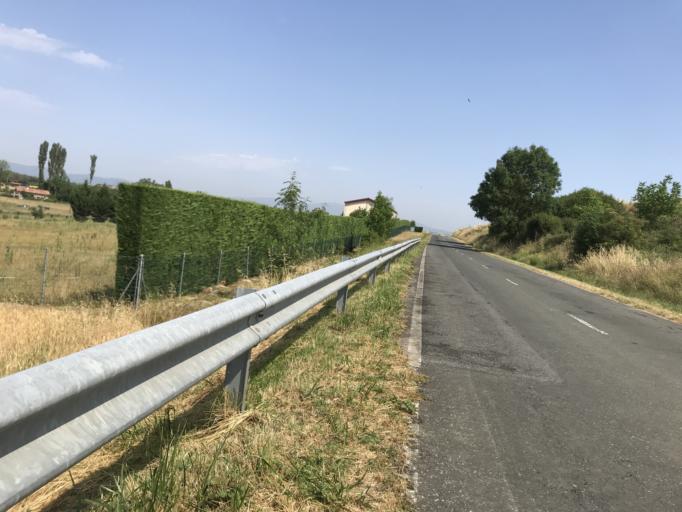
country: ES
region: Basque Country
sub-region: Provincia de Alava
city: Gasteiz / Vitoria
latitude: 42.8201
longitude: -2.6470
